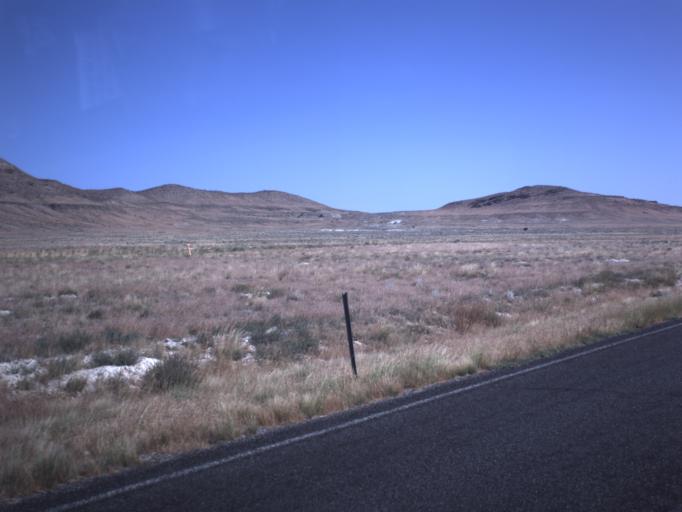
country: US
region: Utah
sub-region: Beaver County
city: Milford
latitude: 38.8567
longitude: -112.8401
